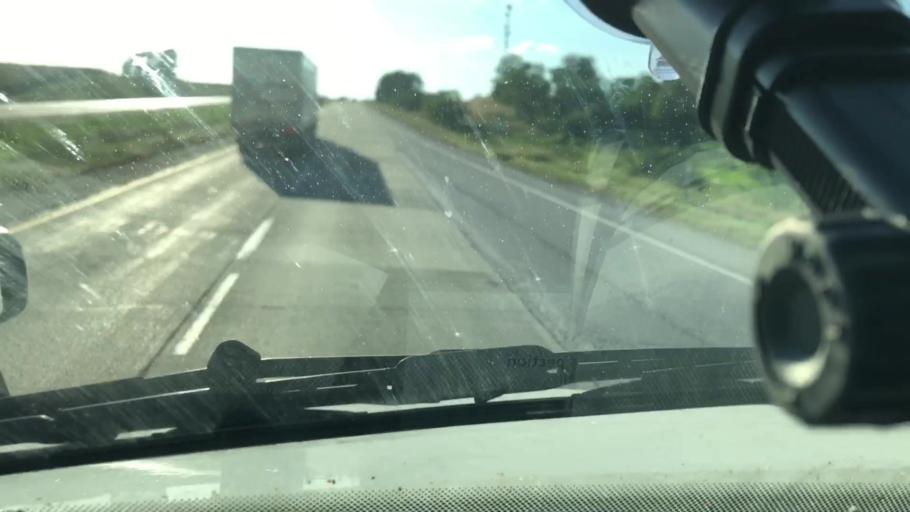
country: US
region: Iowa
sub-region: Pottawattamie County
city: Avoca
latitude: 41.4989
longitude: -95.4569
